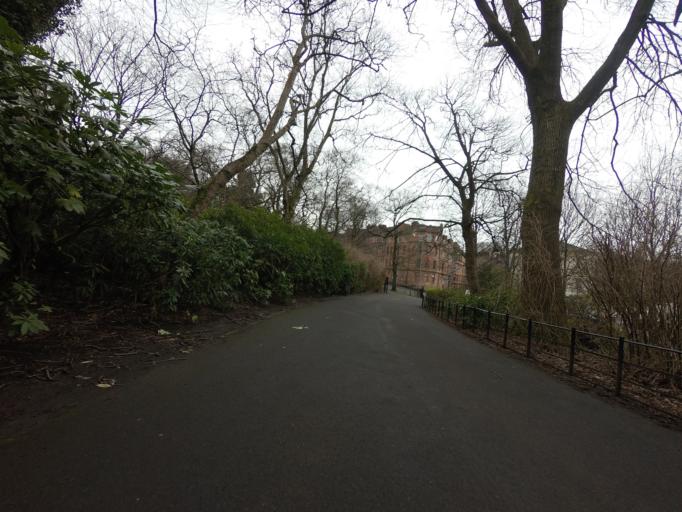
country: GB
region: Scotland
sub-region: East Renfrewshire
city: Giffnock
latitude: 55.8291
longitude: -4.2733
